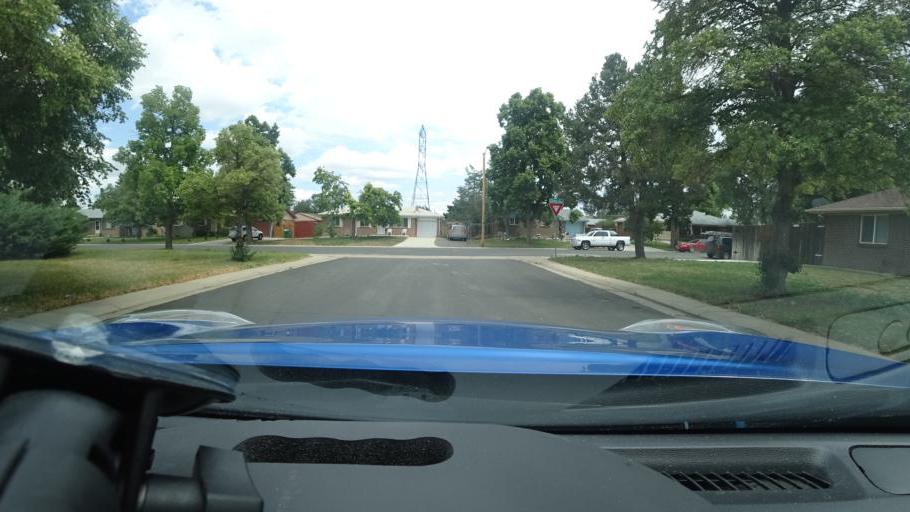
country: US
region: Colorado
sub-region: Adams County
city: Aurora
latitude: 39.7228
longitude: -104.8296
